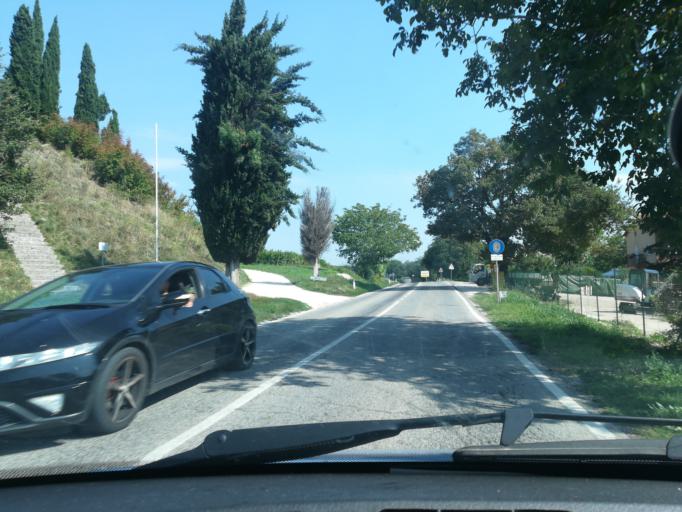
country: IT
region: The Marches
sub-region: Provincia di Macerata
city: Pollenza
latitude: 43.2261
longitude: 13.3406
